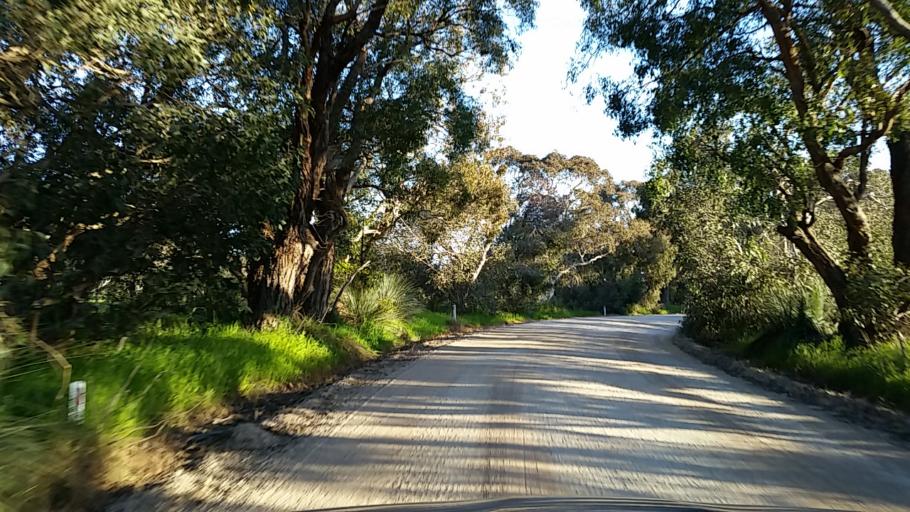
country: AU
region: South Australia
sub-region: Alexandrina
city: Mount Compass
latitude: -35.3128
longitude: 138.6706
